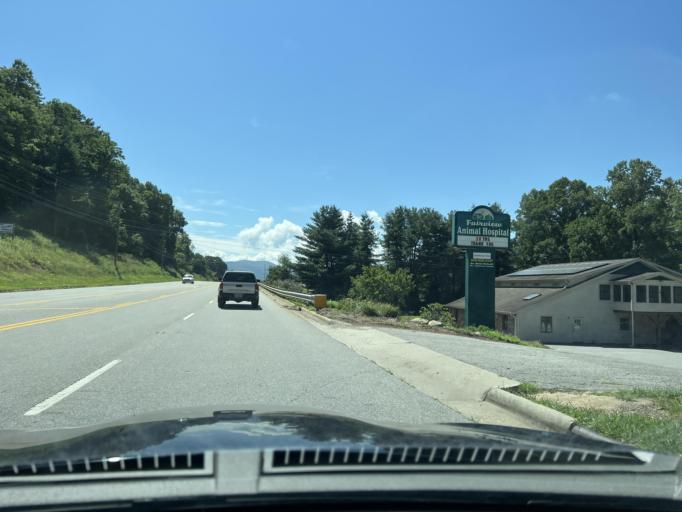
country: US
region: North Carolina
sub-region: Buncombe County
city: Fairview
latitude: 35.5424
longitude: -82.4412
